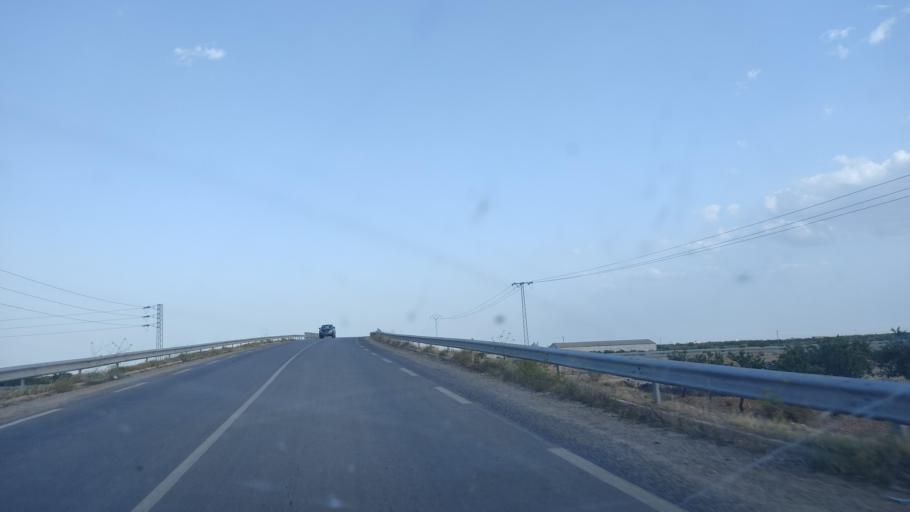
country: TN
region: Safaqis
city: Sfax
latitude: 34.8266
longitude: 10.6421
